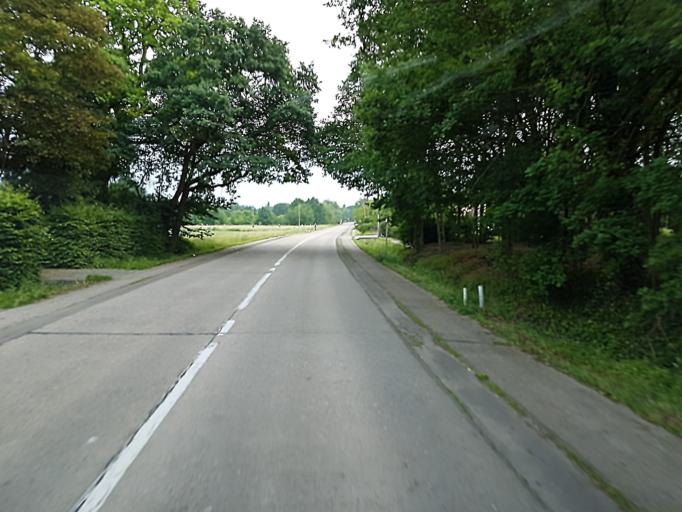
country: BE
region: Flanders
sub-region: Provincie Antwerpen
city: Putte
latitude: 51.0782
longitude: 4.6521
